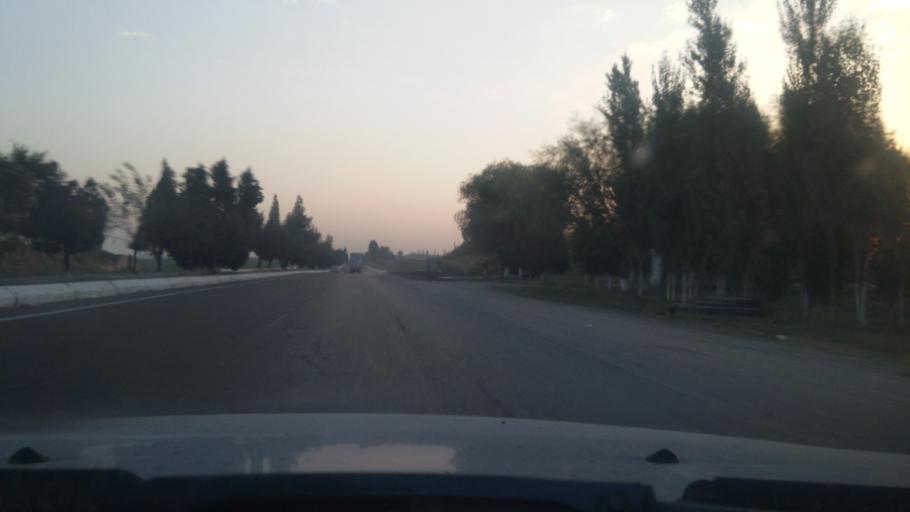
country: UZ
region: Toshkent
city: Zafar
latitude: 41.0414
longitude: 68.8825
